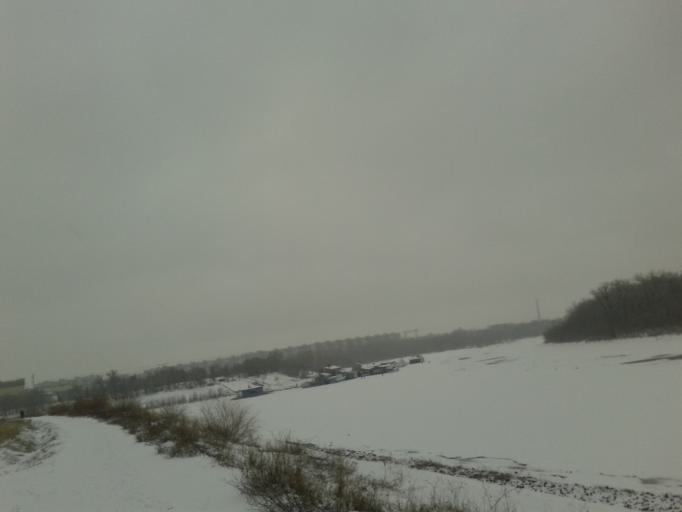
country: RU
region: Volgograd
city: Krasnoslobodsk
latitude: 48.5262
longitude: 44.5548
